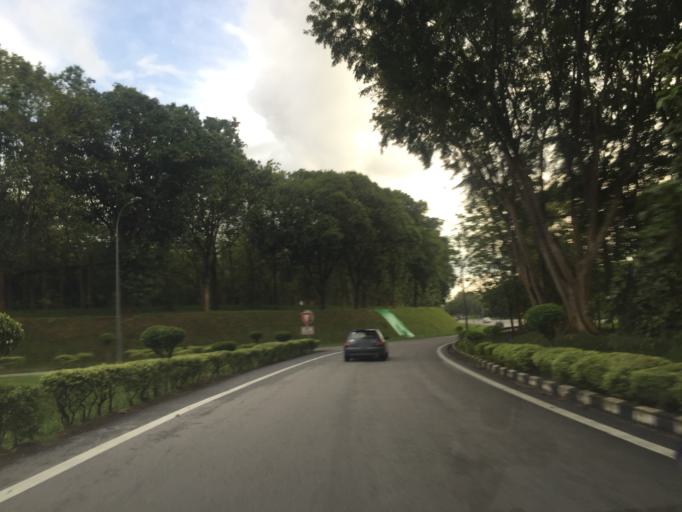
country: MY
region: Kedah
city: Gurun
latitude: 5.8290
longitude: 100.4892
